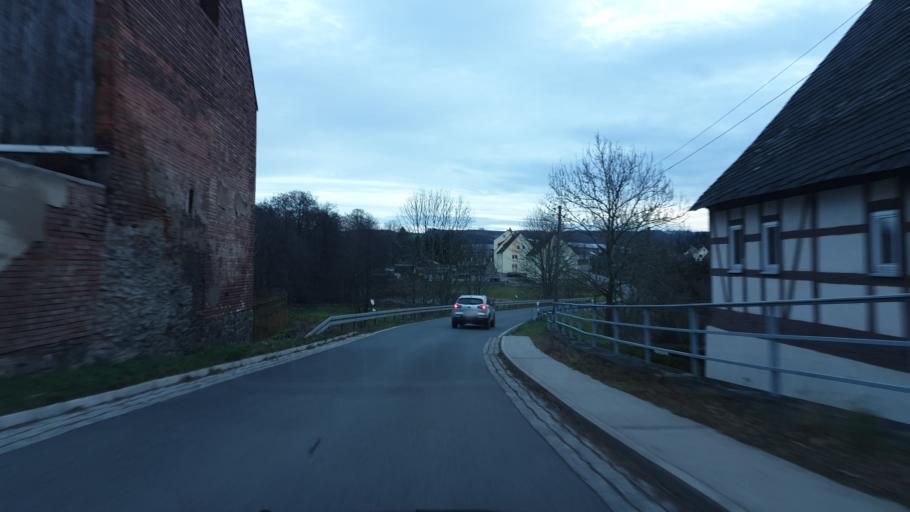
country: DE
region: Saxony
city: Hartenstein
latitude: 50.6760
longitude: 12.6645
